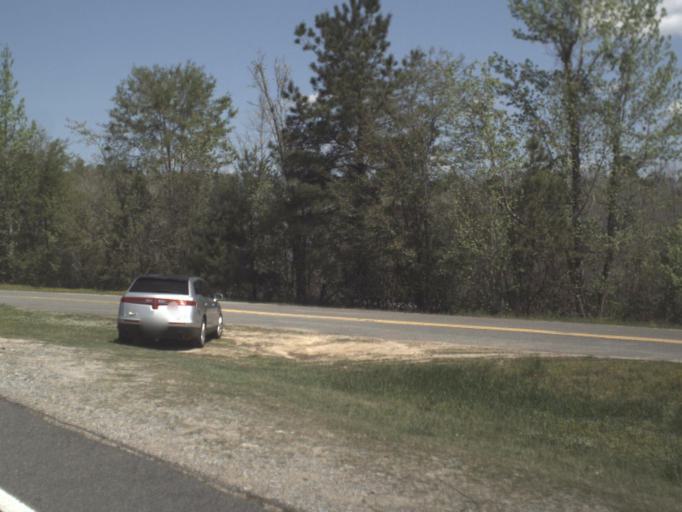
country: US
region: Florida
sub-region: Escambia County
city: Century
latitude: 30.9709
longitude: -87.2399
